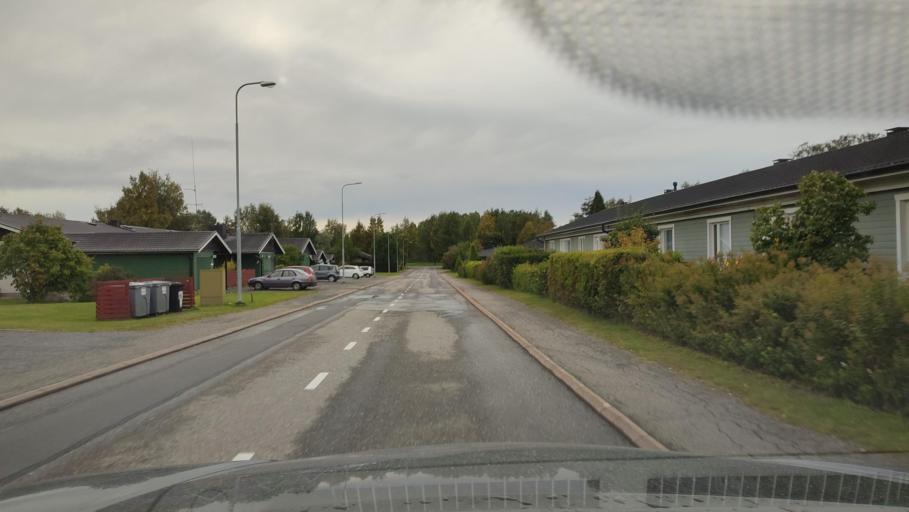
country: FI
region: Ostrobothnia
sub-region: Sydosterbotten
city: Kristinestad
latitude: 62.2798
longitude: 21.3679
